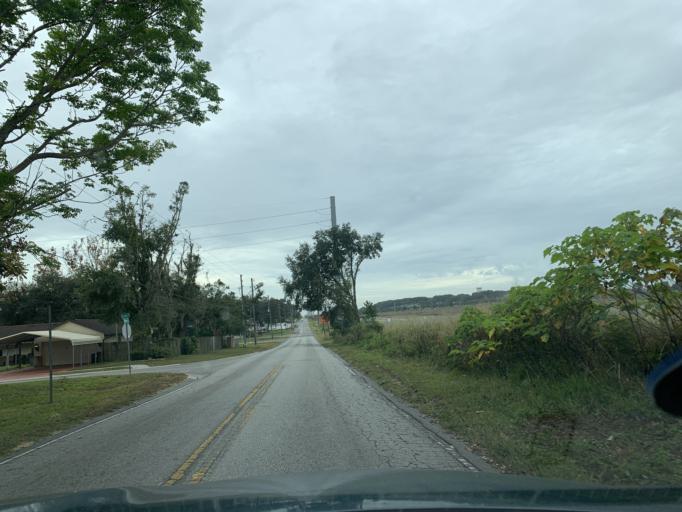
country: US
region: Florida
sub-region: Pasco County
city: Zephyrhills North
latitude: 28.2749
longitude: -82.1798
